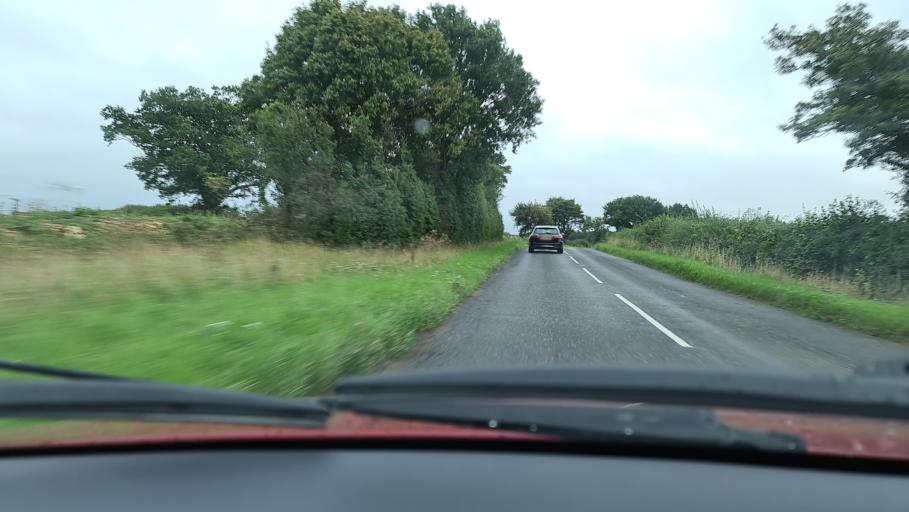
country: GB
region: England
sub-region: Oxfordshire
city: Bicester
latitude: 51.9366
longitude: -1.1987
